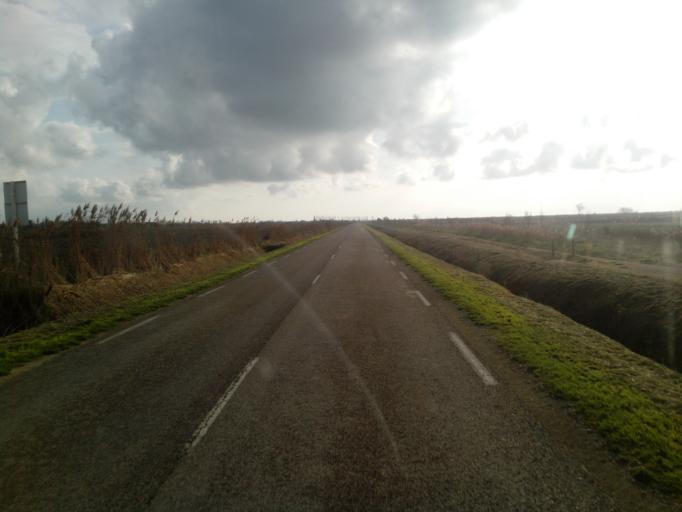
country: FR
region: Provence-Alpes-Cote d'Azur
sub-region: Departement des Bouches-du-Rhone
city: Saint-Martin-de-Crau
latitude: 43.5194
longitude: 4.7064
